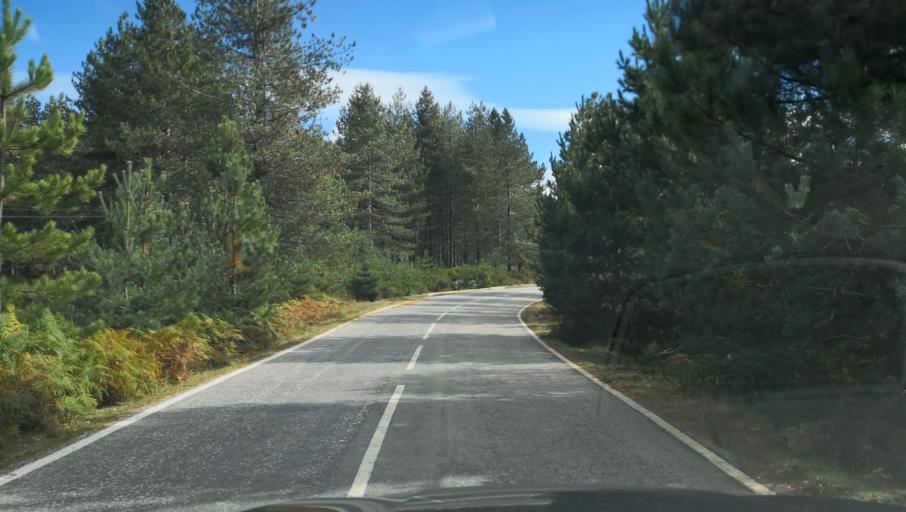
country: PT
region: Vila Real
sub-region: Vila Real
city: Vila Real
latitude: 41.3559
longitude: -7.7927
